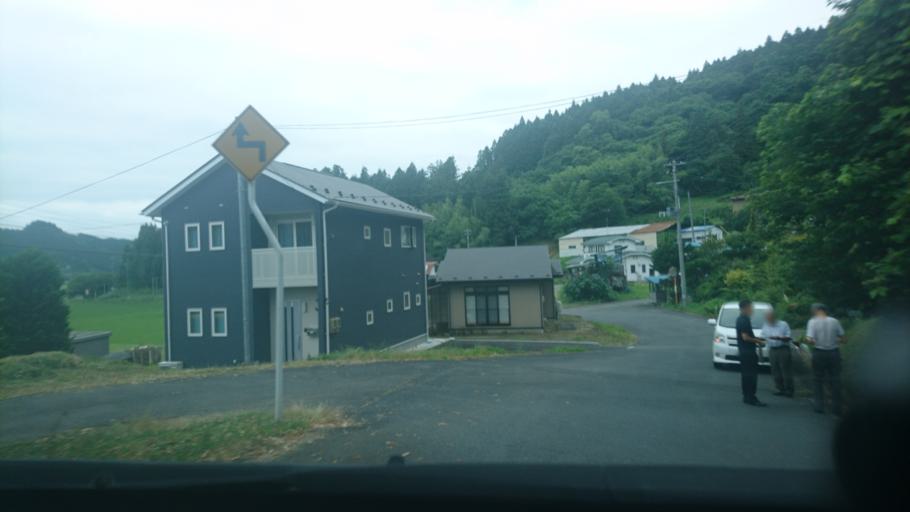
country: JP
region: Iwate
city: Ichinoseki
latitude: 38.9010
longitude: 141.2958
